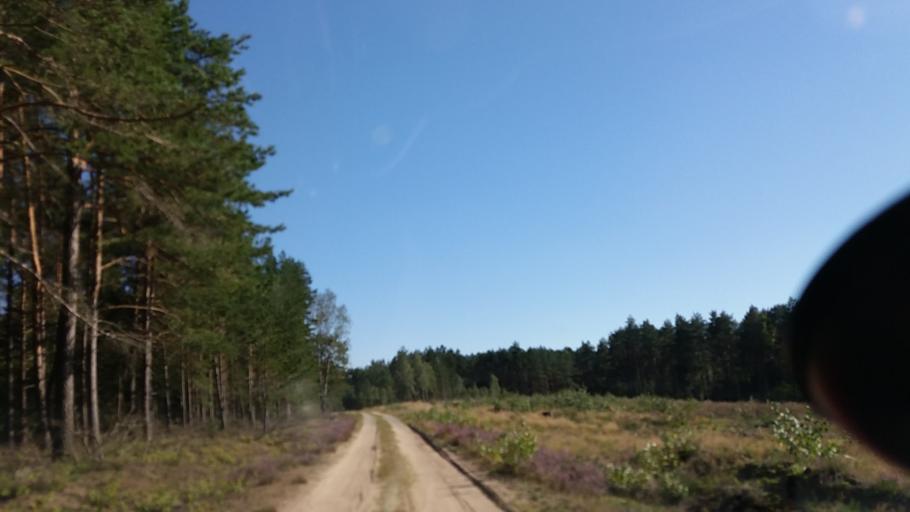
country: PL
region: West Pomeranian Voivodeship
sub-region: Powiat szczecinecki
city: Borne Sulinowo
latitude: 53.5611
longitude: 16.5034
